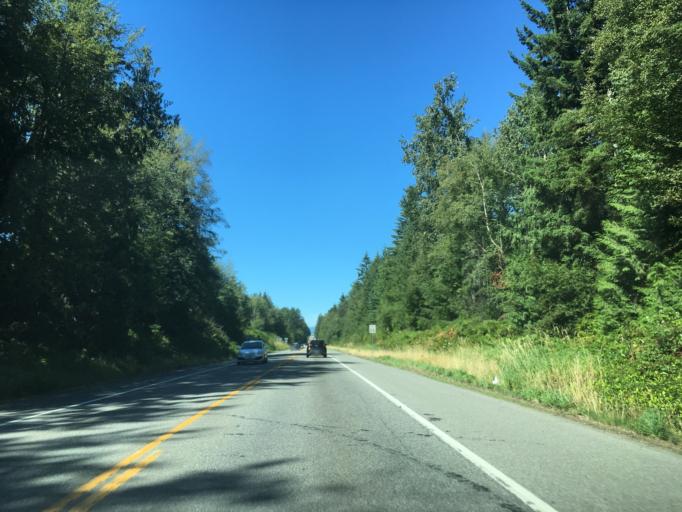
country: US
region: Washington
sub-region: Snohomish County
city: Sisco Heights
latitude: 48.0744
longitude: -122.1114
